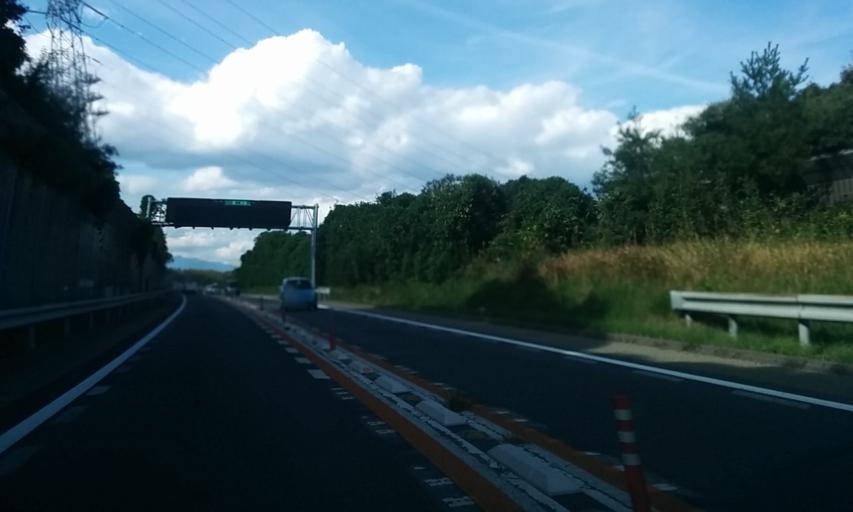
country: JP
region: Kyoto
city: Tanabe
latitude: 34.8264
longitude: 135.7513
